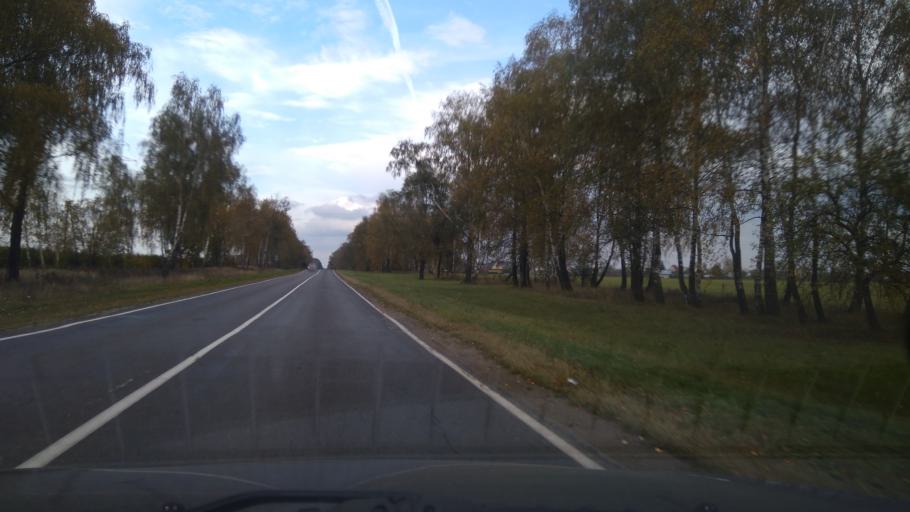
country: BY
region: Minsk
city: Rudzyensk
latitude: 53.6190
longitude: 27.8556
